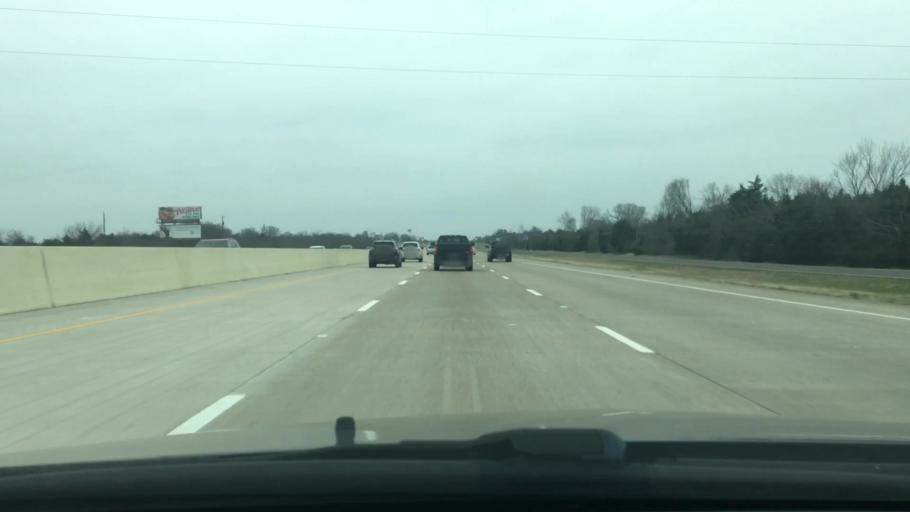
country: US
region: Texas
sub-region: Navarro County
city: Corsicana
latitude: 32.0024
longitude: -96.4316
